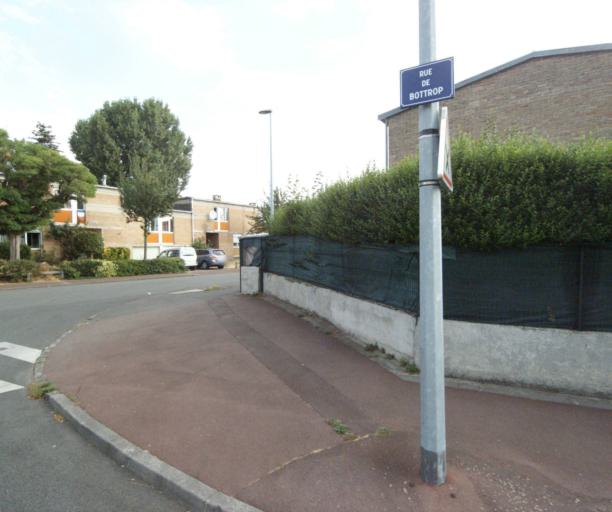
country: FR
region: Nord-Pas-de-Calais
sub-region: Departement du Nord
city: Tourcoing
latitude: 50.7388
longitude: 3.1781
